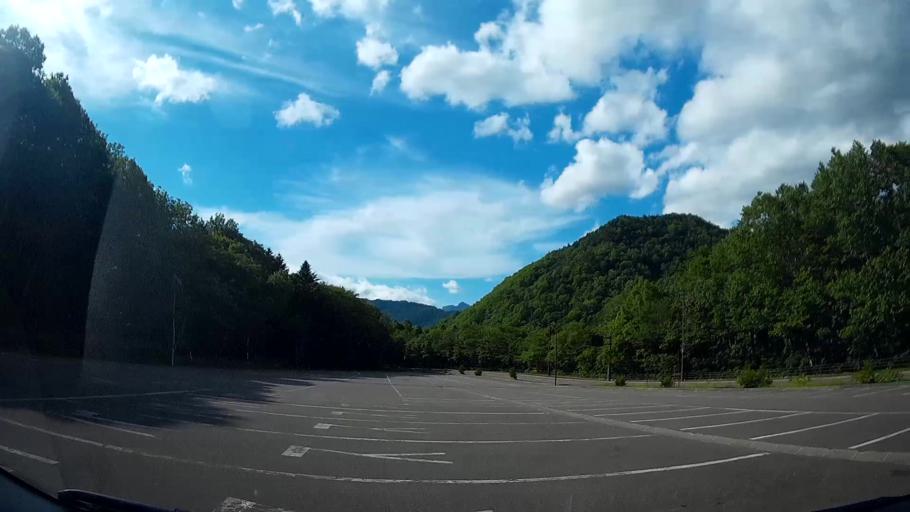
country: JP
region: Hokkaido
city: Sapporo
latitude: 42.9293
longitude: 141.1609
